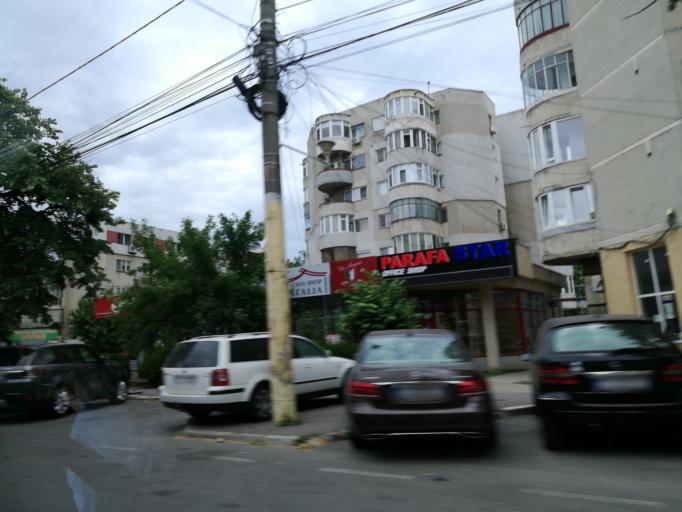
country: RO
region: Constanta
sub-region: Municipiul Constanta
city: Constanta
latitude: 44.1751
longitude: 28.6363
